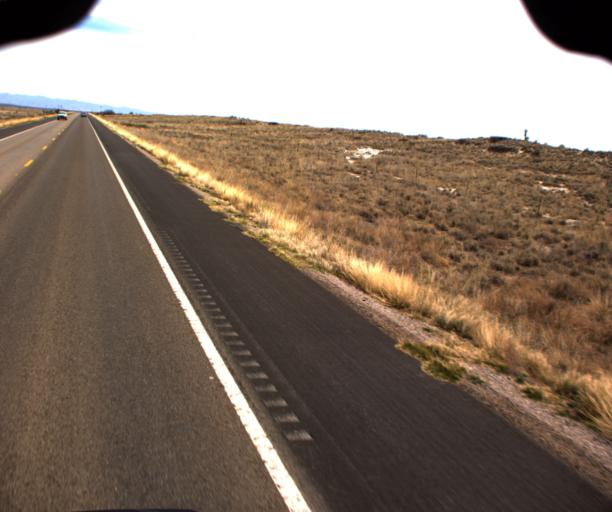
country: US
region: Arizona
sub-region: Cochise County
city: Willcox
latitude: 32.2228
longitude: -109.7923
